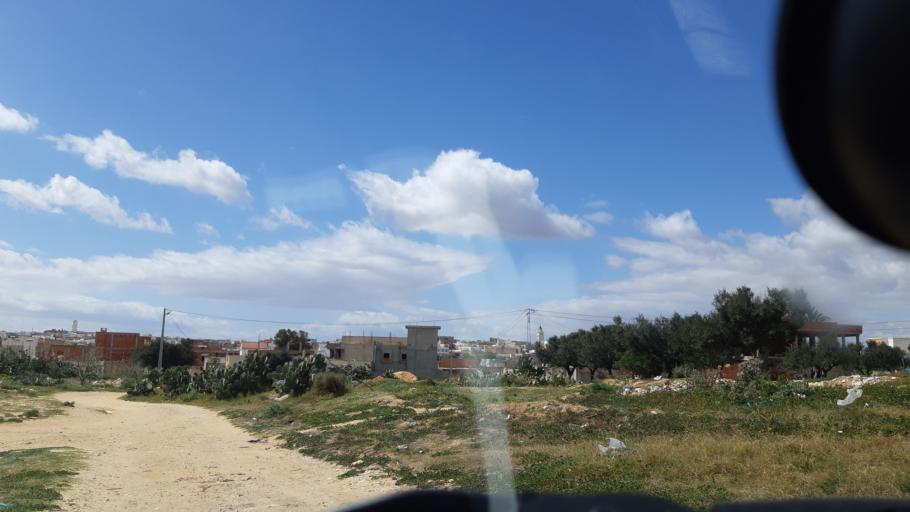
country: TN
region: Susah
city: Akouda
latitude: 35.8804
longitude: 10.5349
